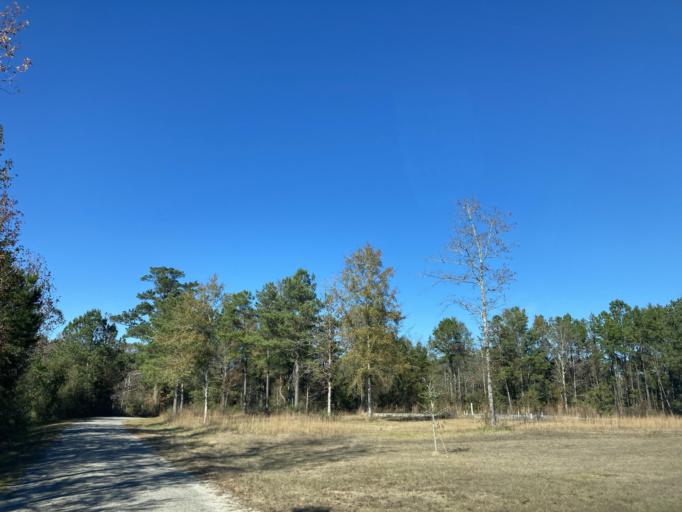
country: US
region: Mississippi
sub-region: Lamar County
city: Sumrall
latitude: 31.3002
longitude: -89.6382
